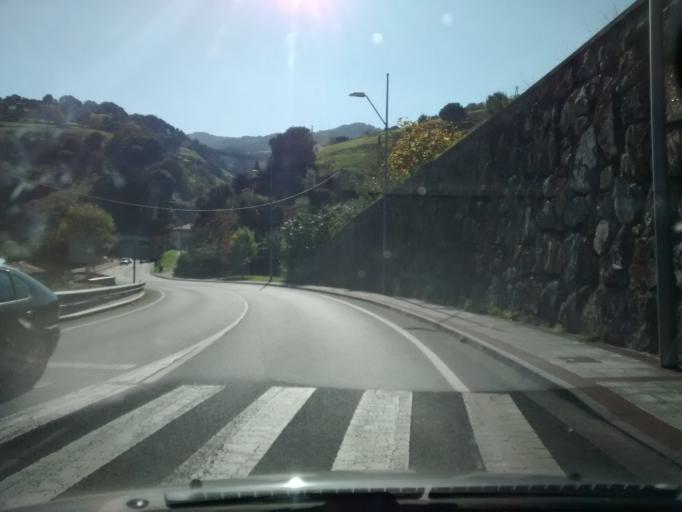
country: ES
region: Basque Country
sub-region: Provincia de Guipuzcoa
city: Deba
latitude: 43.2906
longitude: -2.3636
